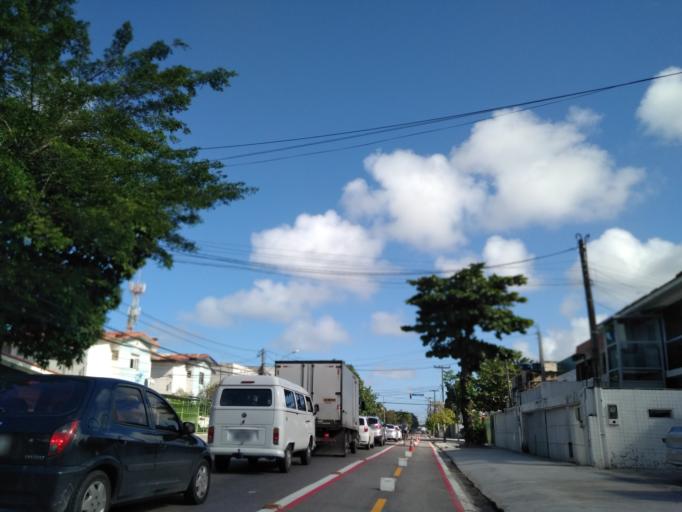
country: BR
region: Pernambuco
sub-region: Recife
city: Recife
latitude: -8.0903
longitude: -34.9106
